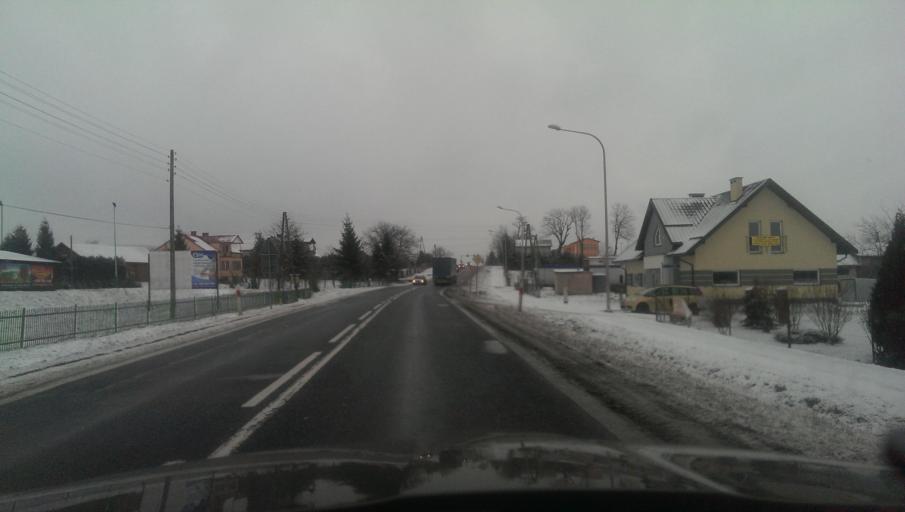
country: PL
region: Subcarpathian Voivodeship
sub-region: Powiat sanocki
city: Dlugie
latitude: 49.5777
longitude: 22.0449
